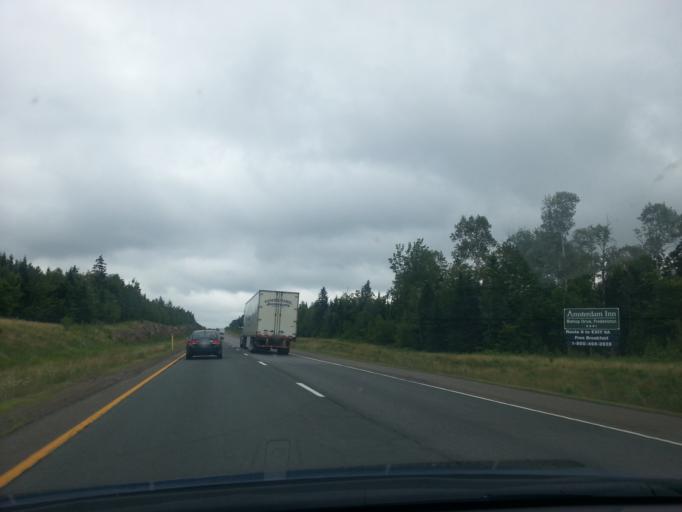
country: CA
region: New Brunswick
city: Fredericton
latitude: 45.8917
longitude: -66.7924
